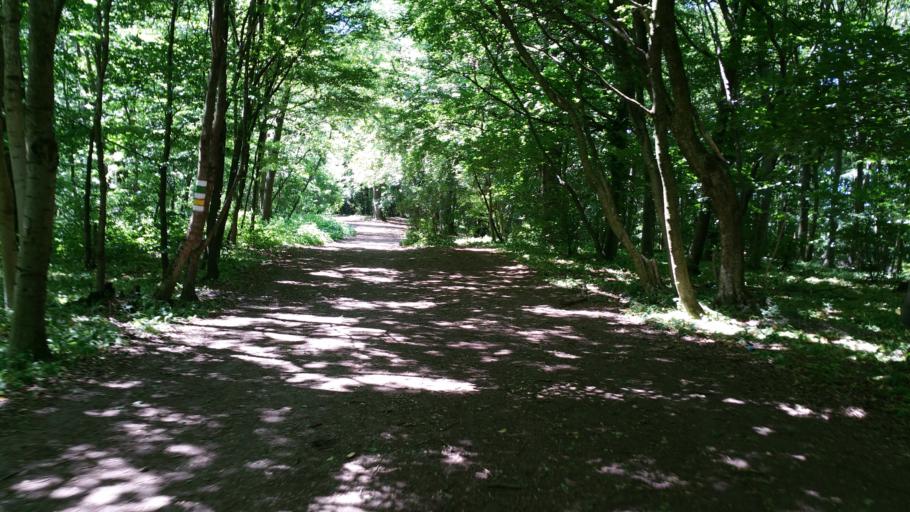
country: AT
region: Lower Austria
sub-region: Politischer Bezirk Wien-Umgebung
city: Purkersdorf
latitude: 48.2238
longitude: 16.2697
